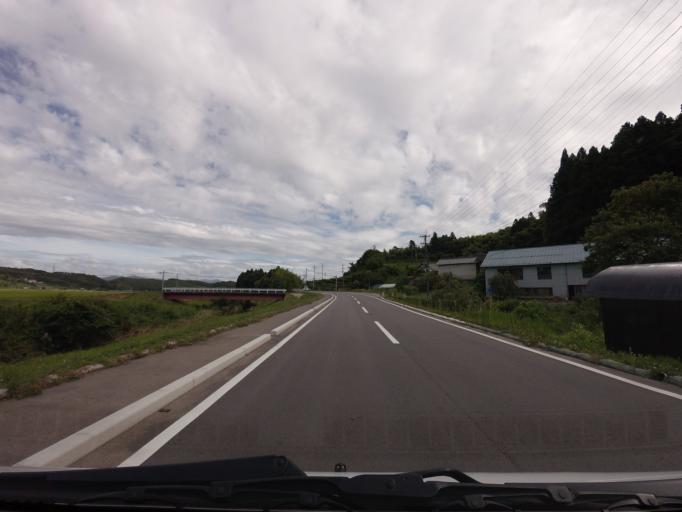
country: JP
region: Fukushima
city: Nihommatsu
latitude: 37.6632
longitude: 140.4215
